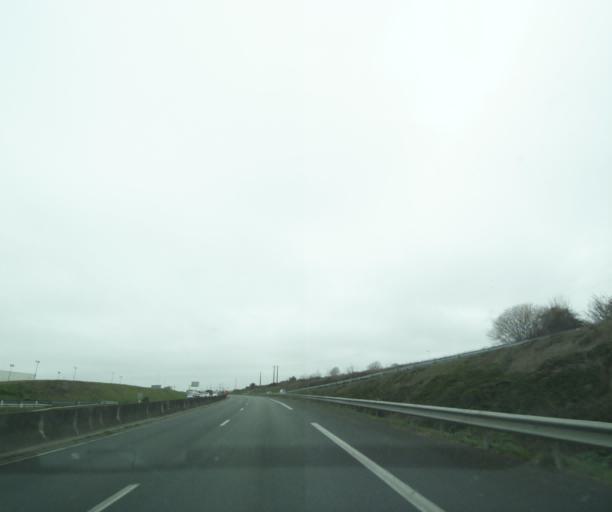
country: FR
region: Poitou-Charentes
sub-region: Departement de la Charente-Maritime
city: Perigny
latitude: 46.1539
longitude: -1.1142
